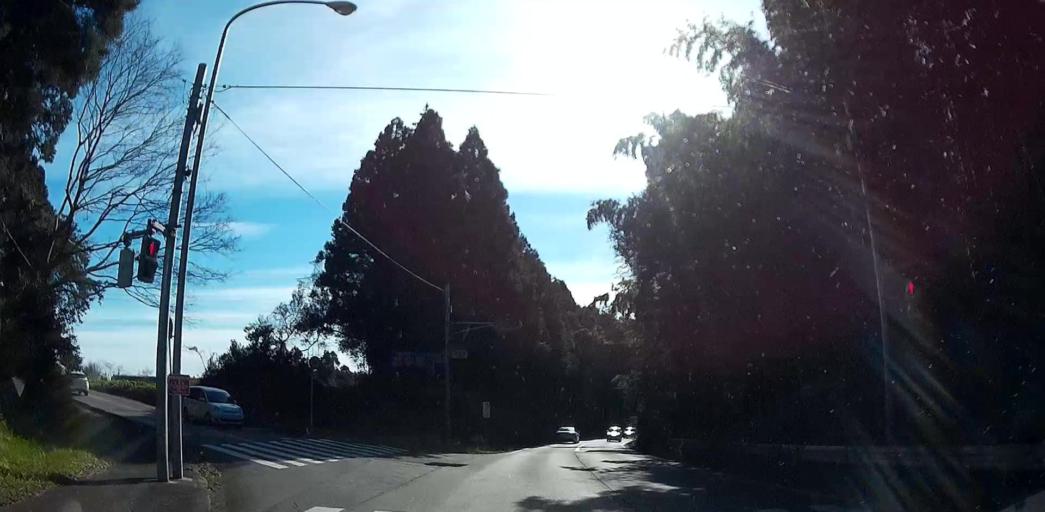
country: JP
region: Chiba
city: Yokaichiba
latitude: 35.7492
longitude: 140.4572
